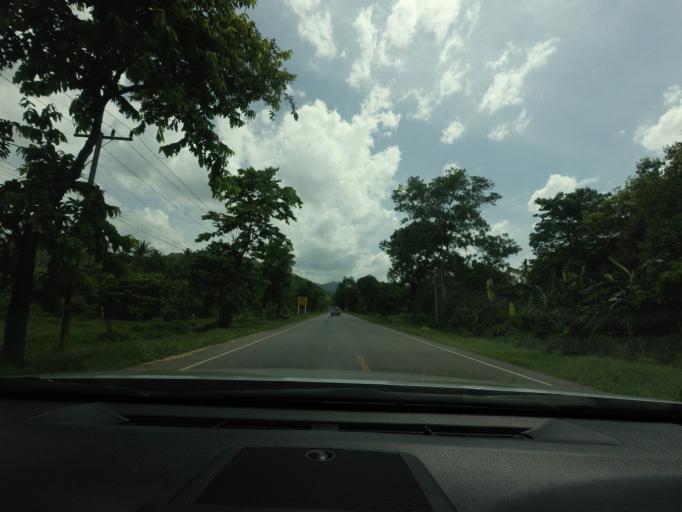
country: TH
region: Yala
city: Raman
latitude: 6.4543
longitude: 101.3506
